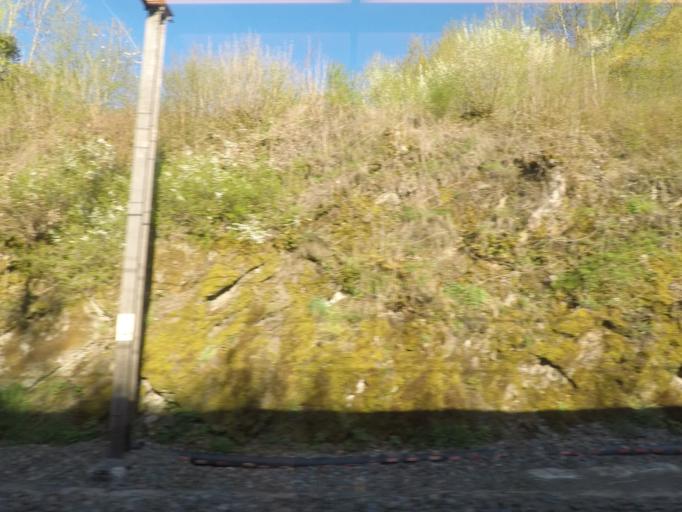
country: BE
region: Wallonia
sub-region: Province du Luxembourg
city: Tellin
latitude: 50.0932
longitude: 5.2834
